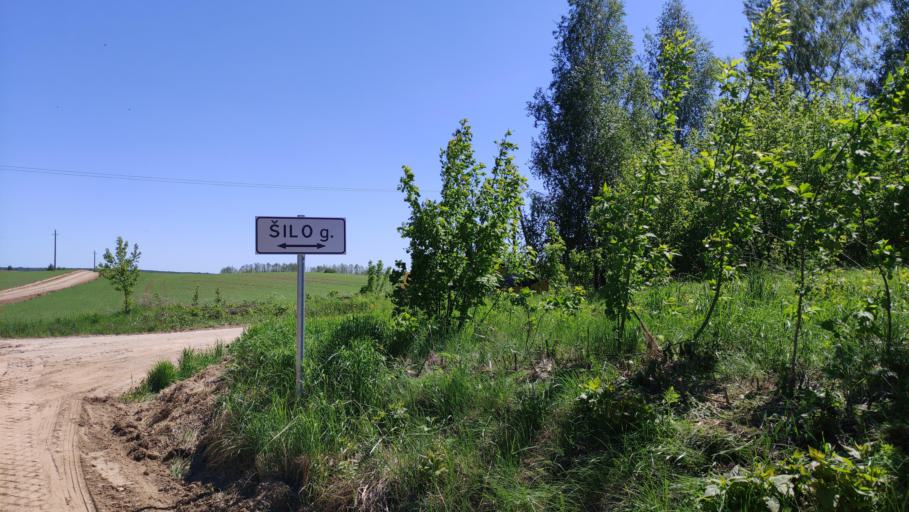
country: LT
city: Simnas
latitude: 54.3136
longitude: 23.8061
